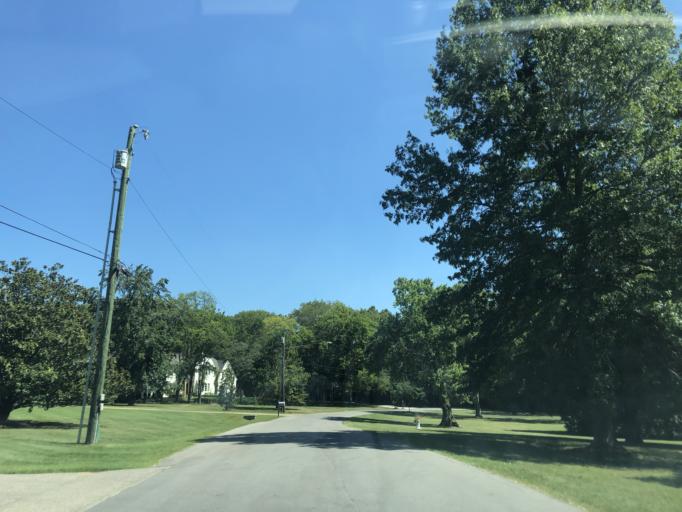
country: US
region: Tennessee
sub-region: Davidson County
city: Forest Hills
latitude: 36.0639
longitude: -86.8315
